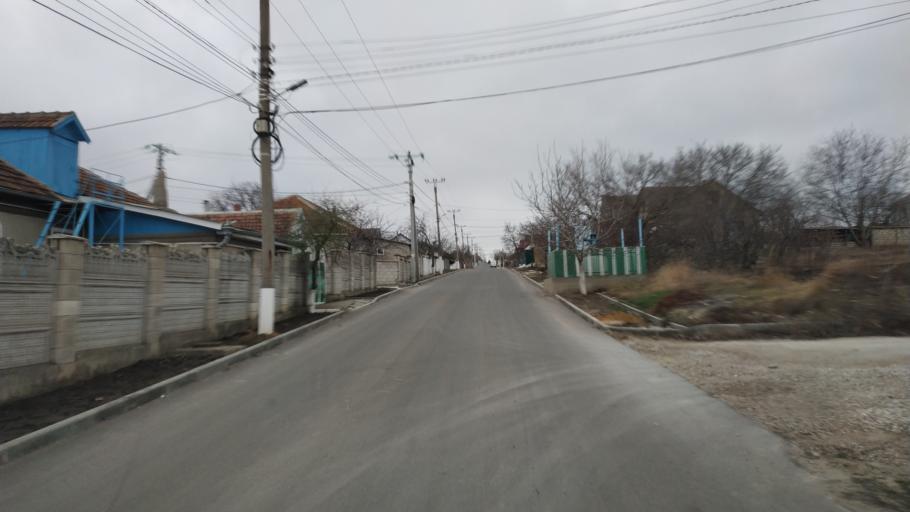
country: MD
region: Laloveni
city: Ialoveni
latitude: 46.9096
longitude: 28.8022
